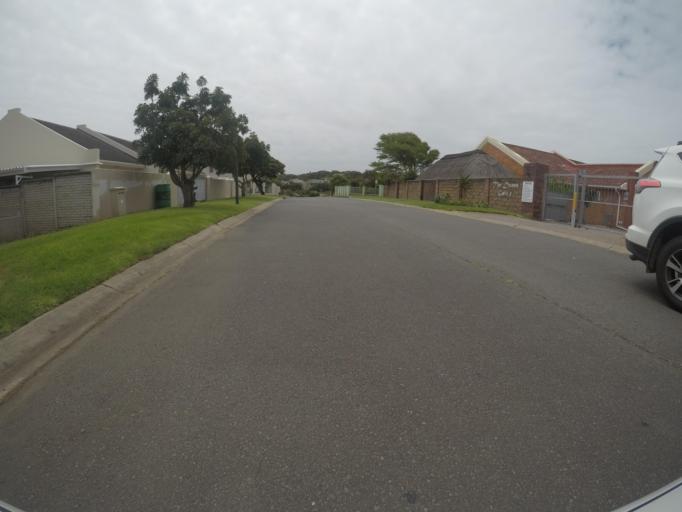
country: ZA
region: Eastern Cape
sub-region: Buffalo City Metropolitan Municipality
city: East London
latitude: -32.9784
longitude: 27.9553
